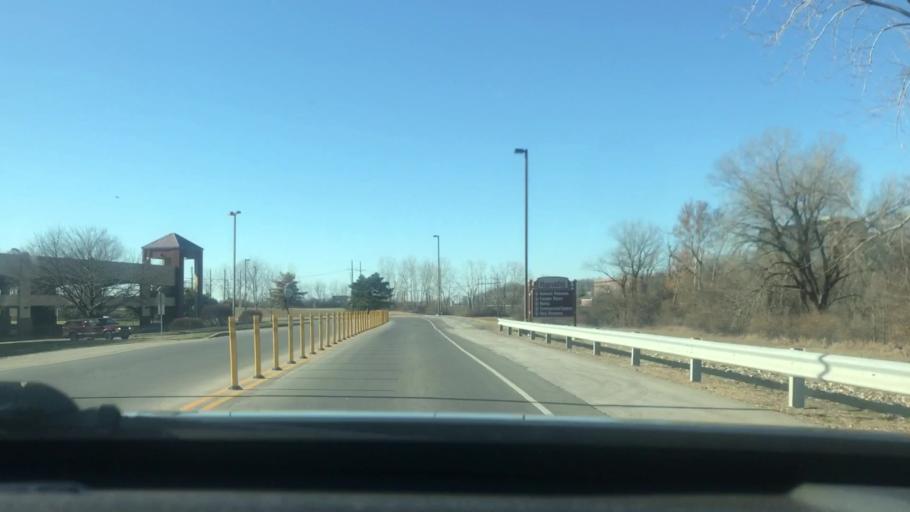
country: US
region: Missouri
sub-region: Clay County
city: North Kansas City
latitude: 39.1444
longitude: -94.5440
